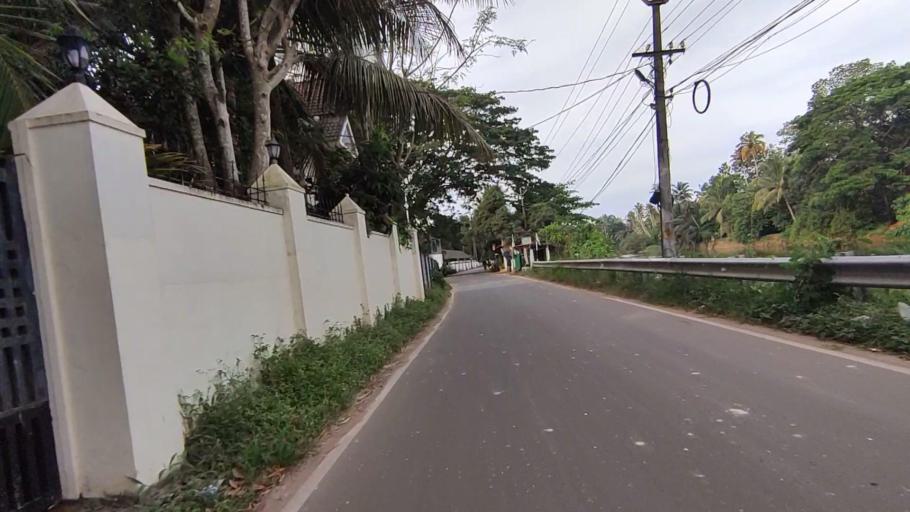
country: IN
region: Kerala
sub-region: Kottayam
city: Kottayam
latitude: 9.5970
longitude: 76.5028
